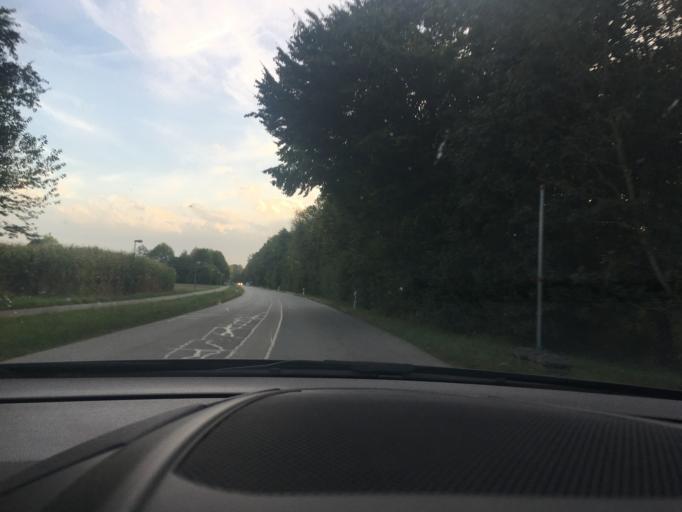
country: DE
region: Bavaria
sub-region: Upper Bavaria
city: Ismaning
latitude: 48.2447
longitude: 11.6860
